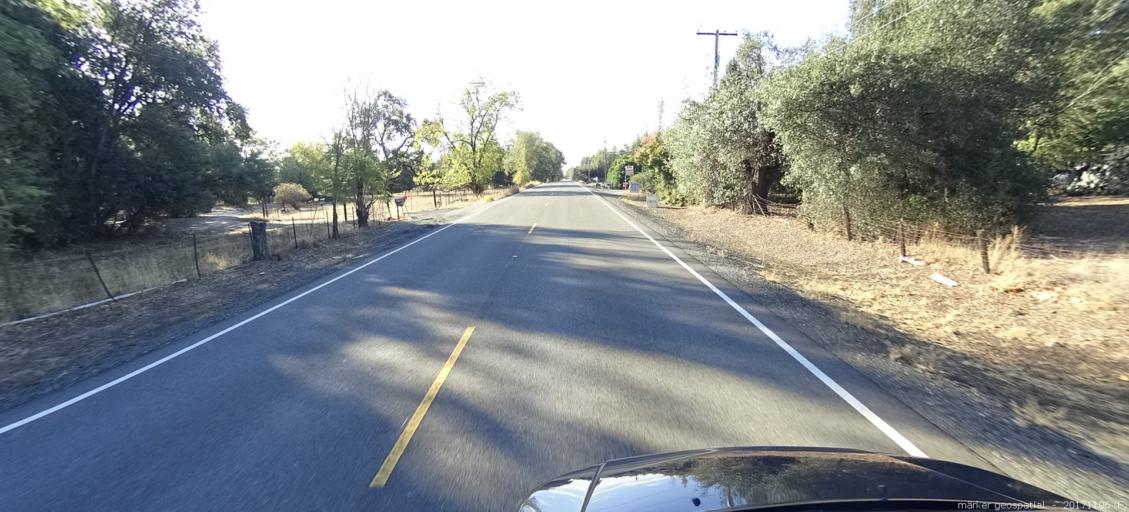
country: US
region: California
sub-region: Shasta County
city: Bella Vista
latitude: 40.6111
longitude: -122.2347
